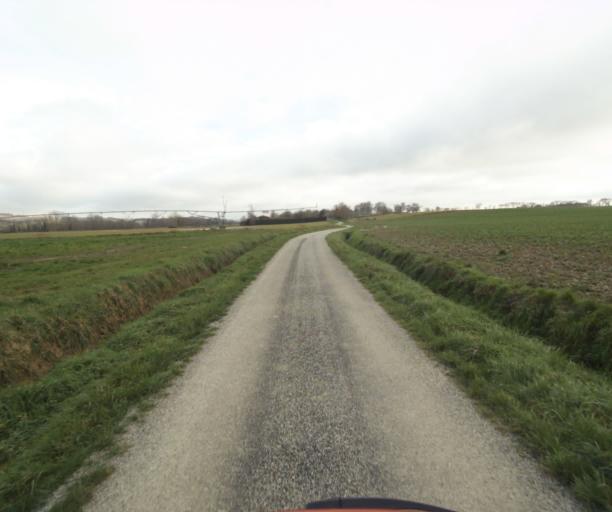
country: FR
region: Midi-Pyrenees
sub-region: Departement de l'Ariege
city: Mazeres
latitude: 43.2323
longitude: 1.7100
